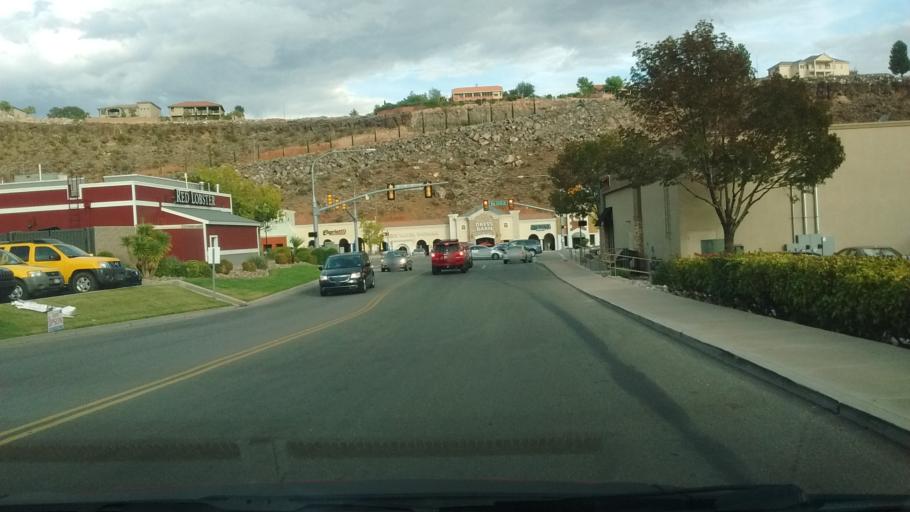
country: US
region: Utah
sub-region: Washington County
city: Saint George
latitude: 37.1120
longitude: -113.5550
